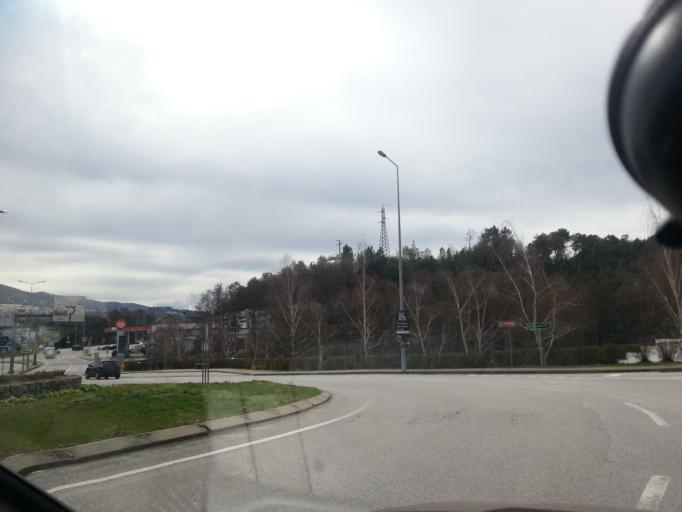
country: PT
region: Guarda
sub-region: Seia
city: Seia
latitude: 40.4325
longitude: -7.7187
